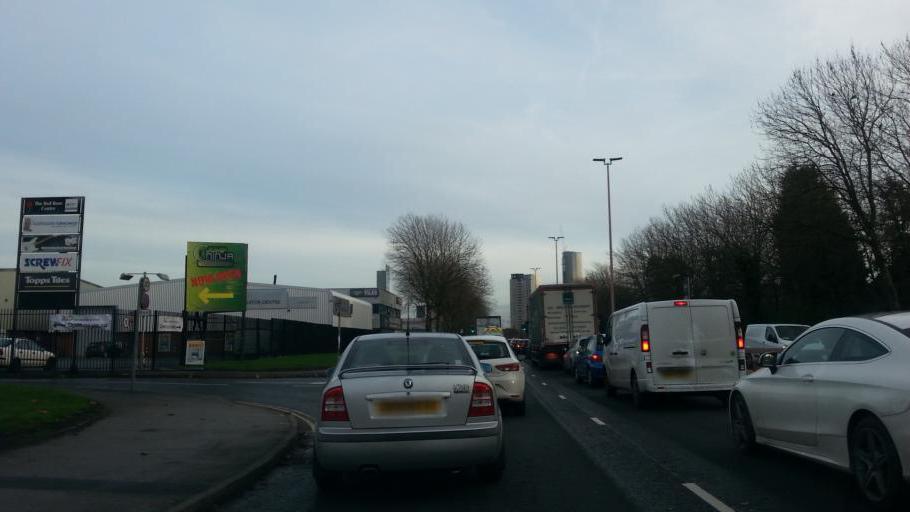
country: GB
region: England
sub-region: City and Borough of Salford
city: Salford
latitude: 53.4776
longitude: -2.2744
